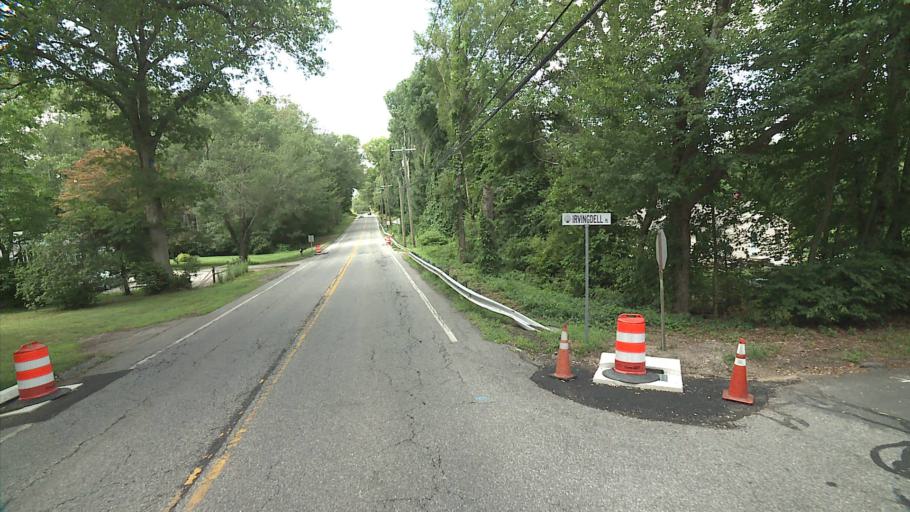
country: US
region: Connecticut
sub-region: New London County
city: Niantic
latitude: 41.3784
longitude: -72.2148
